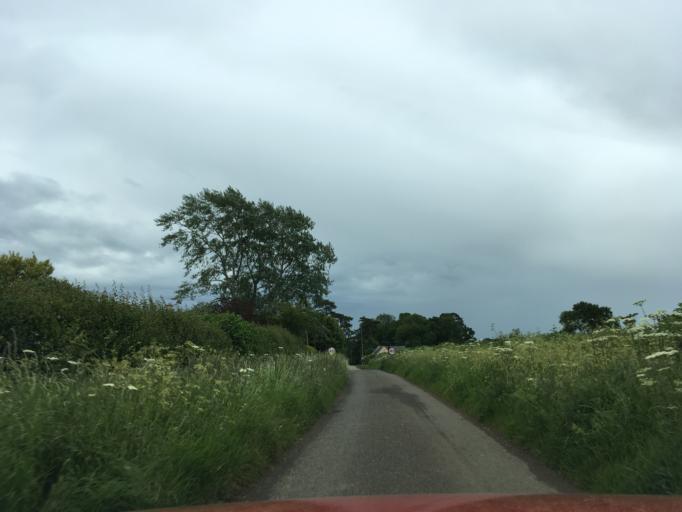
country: GB
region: England
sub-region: Wiltshire
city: Norton
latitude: 51.5854
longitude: -2.2011
